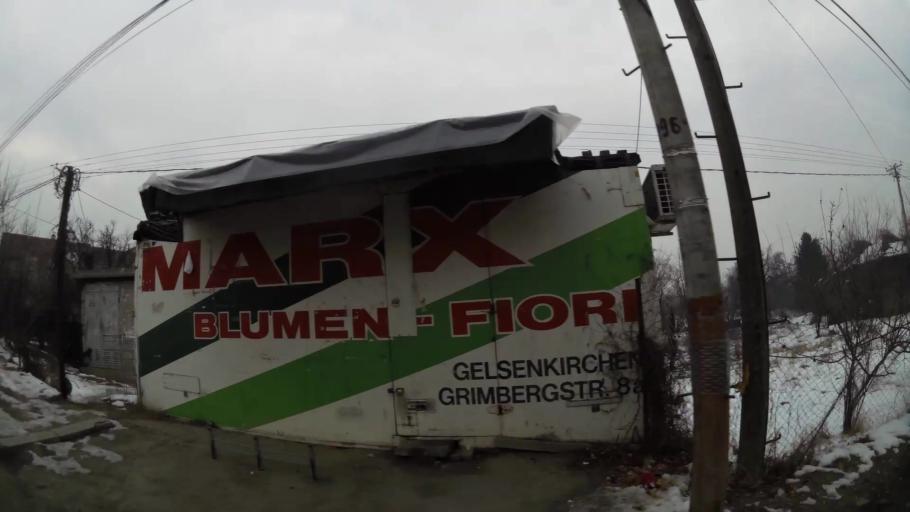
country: MK
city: Kondovo
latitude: 42.0458
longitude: 21.3465
